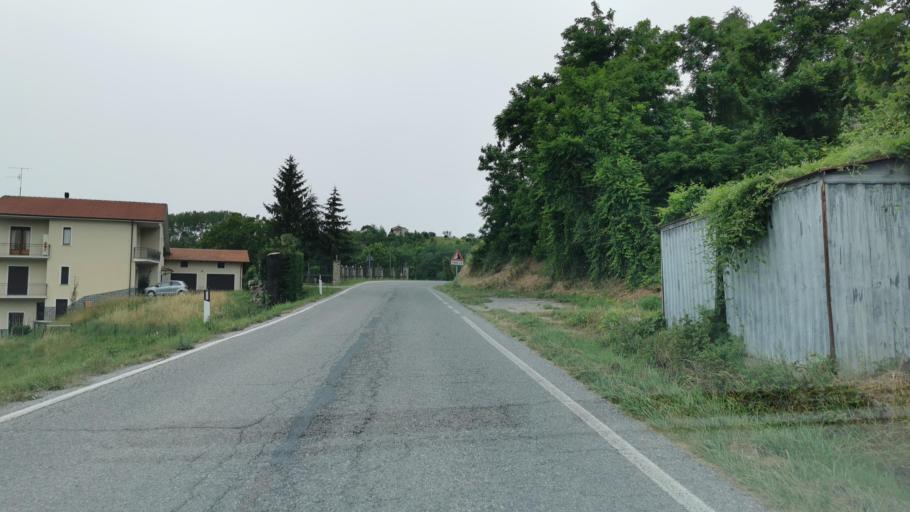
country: IT
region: Piedmont
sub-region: Provincia di Cuneo
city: Sale San Giovanni
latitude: 44.3983
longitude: 8.0790
